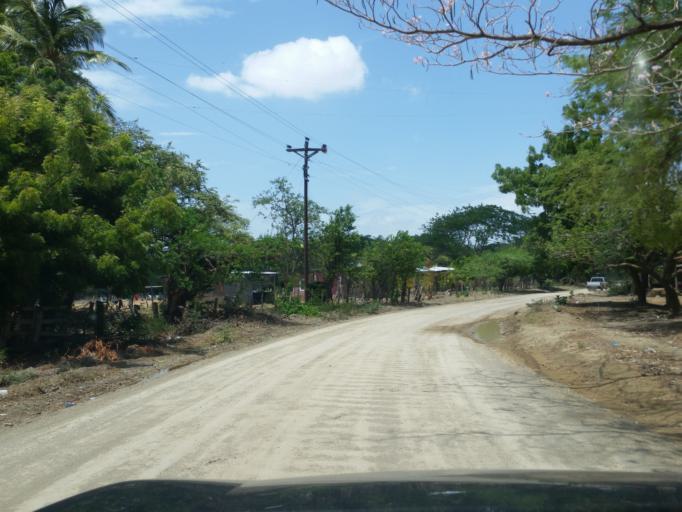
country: NI
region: Rivas
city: Tola
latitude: 11.4554
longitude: -86.0729
